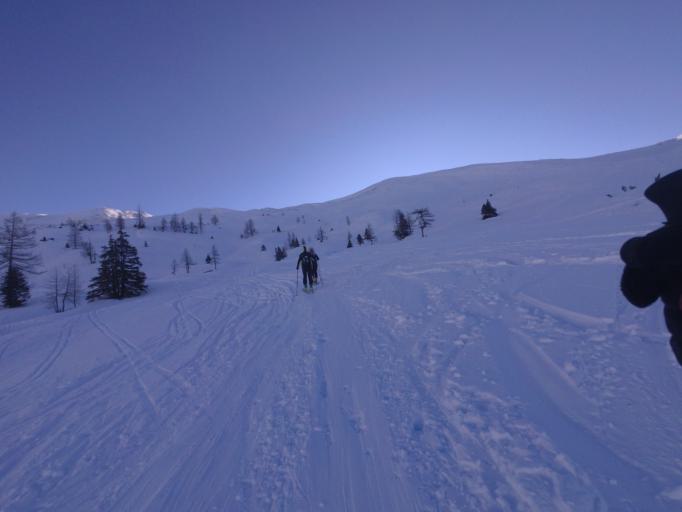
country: AT
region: Salzburg
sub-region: Politischer Bezirk Sankt Johann im Pongau
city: Huttschlag
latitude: 47.1771
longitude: 13.2975
